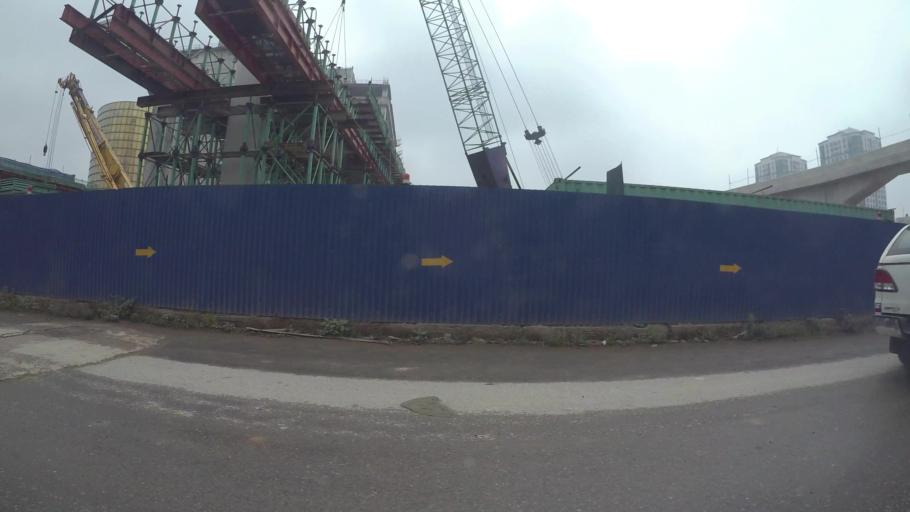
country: VN
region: Ha Noi
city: Cau Dien
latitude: 21.0529
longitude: 105.7817
